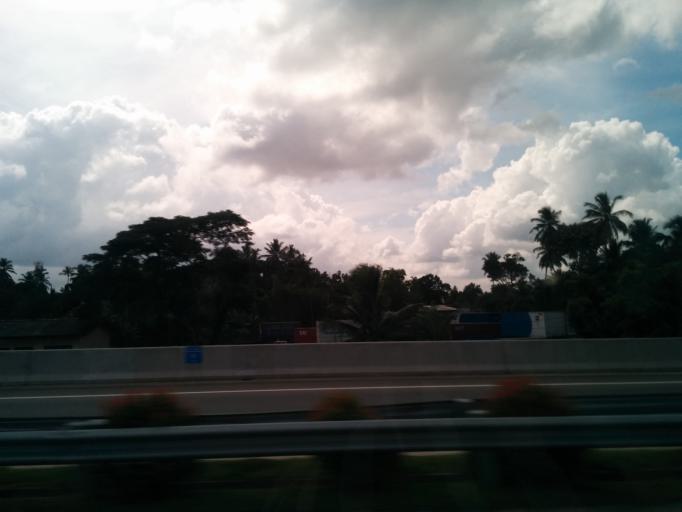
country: LK
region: Western
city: Wattala
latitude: 6.9829
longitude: 79.8992
